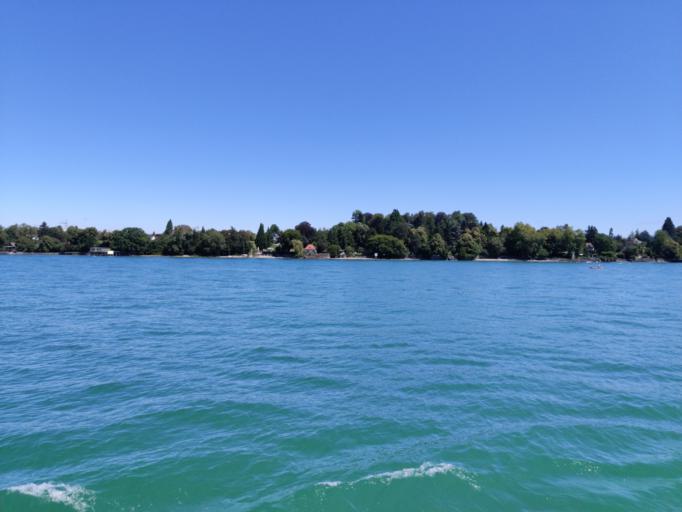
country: DE
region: Bavaria
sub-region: Swabia
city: Bodolz
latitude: 47.5545
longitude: 9.6495
